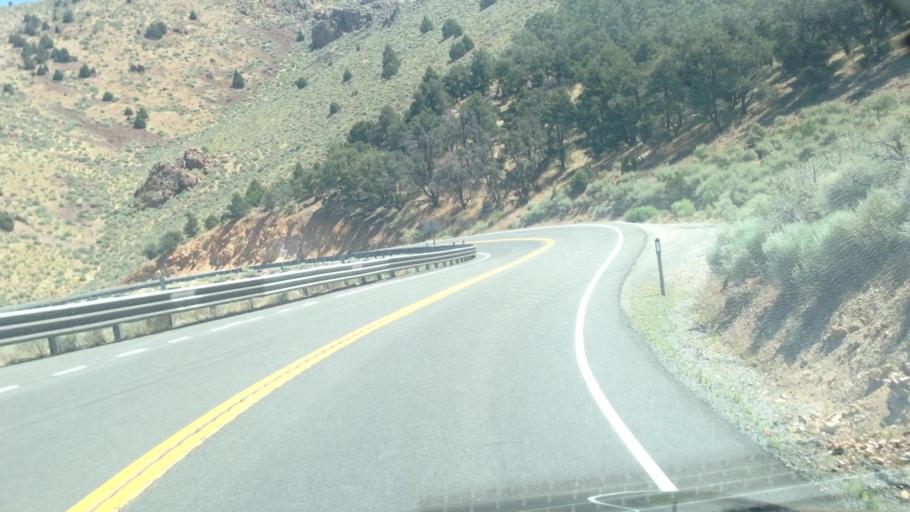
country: US
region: Nevada
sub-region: Storey County
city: Virginia City
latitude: 39.3761
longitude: -119.6941
